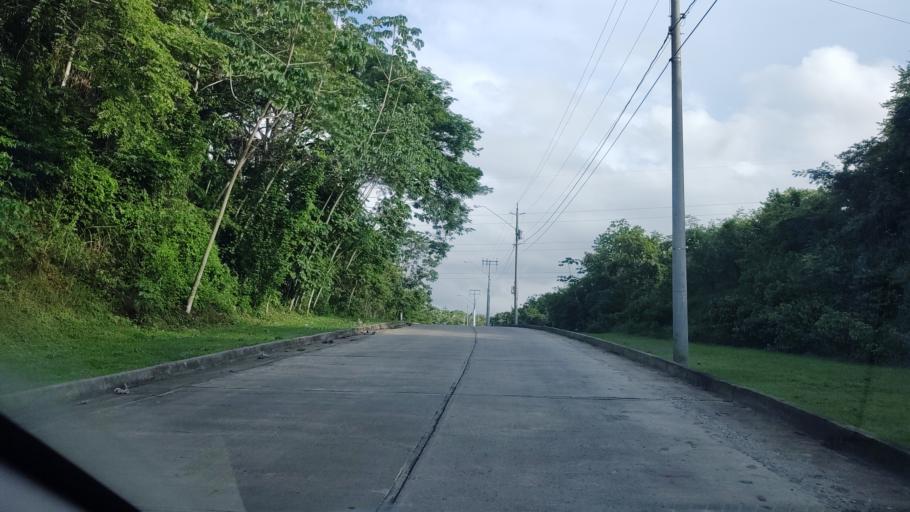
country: PA
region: Panama
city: Nuevo Arraijan
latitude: 8.9234
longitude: -79.7515
